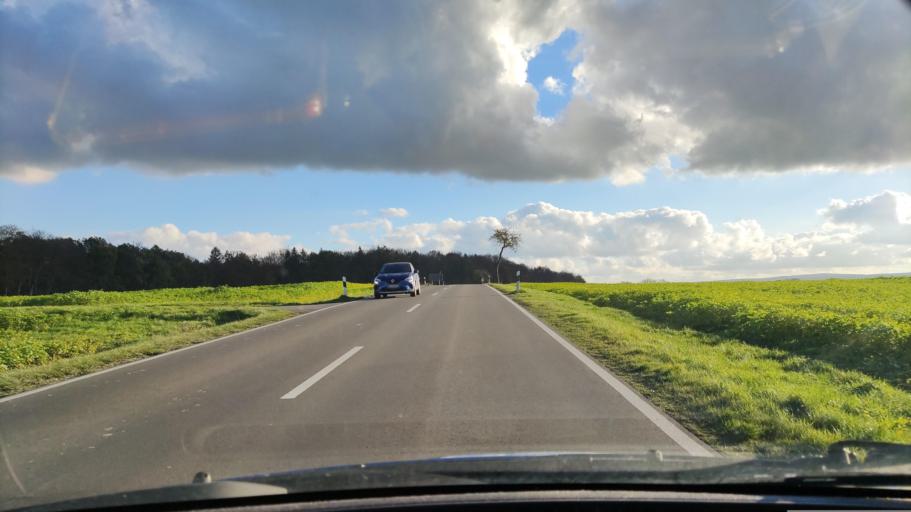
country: DE
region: Lower Saxony
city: Holenberg
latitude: 51.9096
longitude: 9.6114
